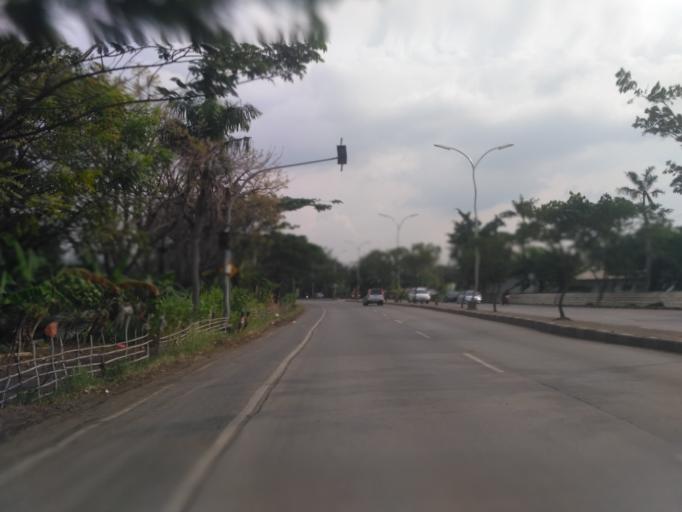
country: ID
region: Central Java
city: Semarang
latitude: -6.9721
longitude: 110.3892
